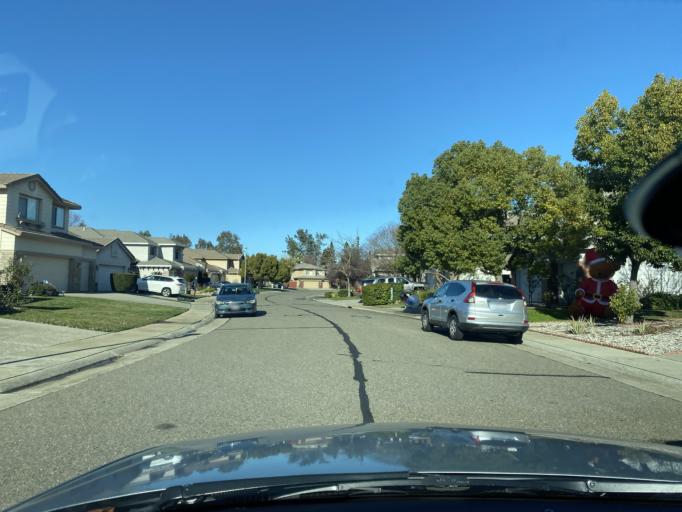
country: US
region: California
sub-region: Sacramento County
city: Laguna
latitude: 38.4348
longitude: -121.3945
